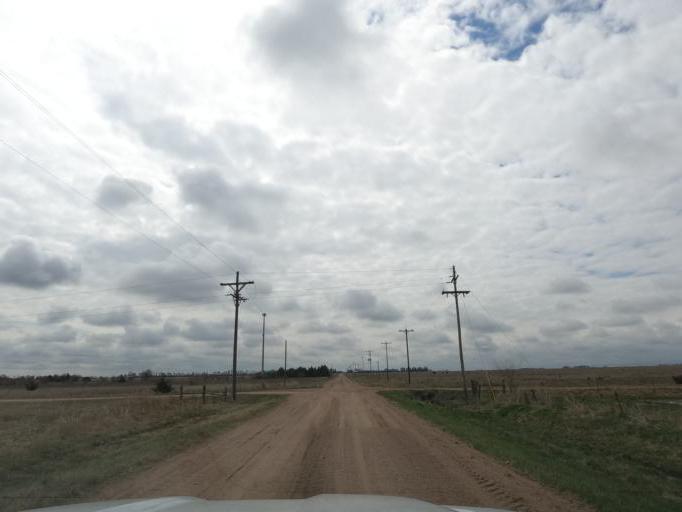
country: US
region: Kansas
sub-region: Reno County
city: South Hutchinson
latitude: 37.9412
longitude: -98.0319
